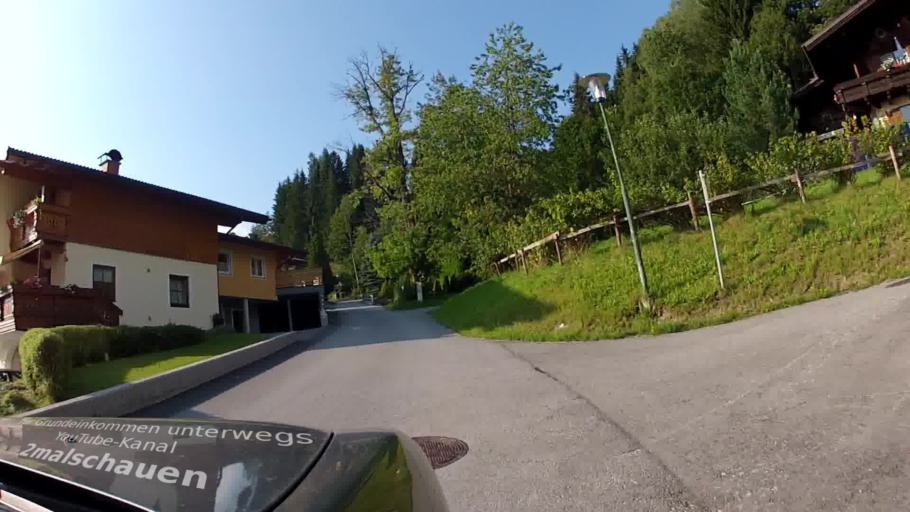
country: AT
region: Salzburg
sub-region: Politischer Bezirk Sankt Johann im Pongau
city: Eben im Pongau
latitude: 47.4235
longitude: 13.3823
